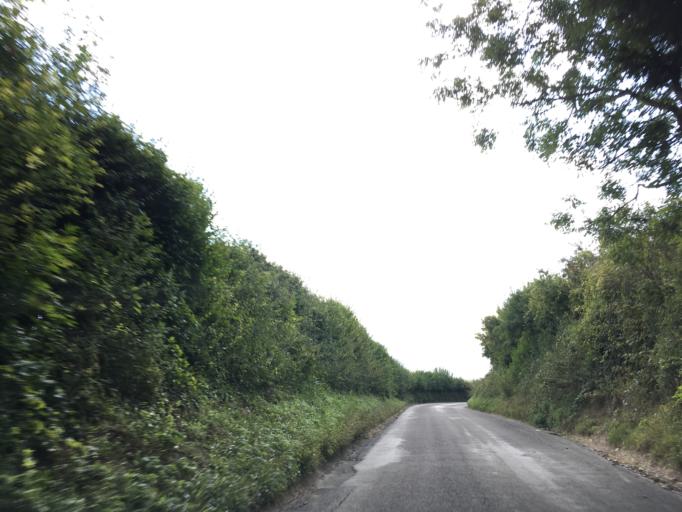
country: GB
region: England
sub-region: Hampshire
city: Andover
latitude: 51.1904
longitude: -1.3790
